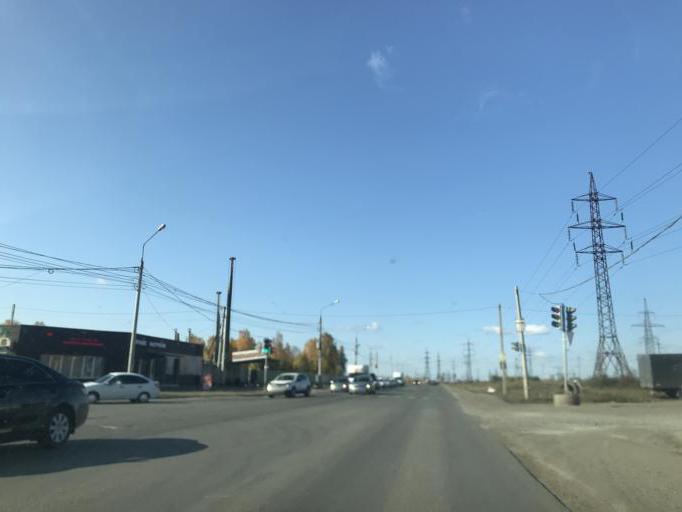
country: RU
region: Chelyabinsk
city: Roshchino
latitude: 55.2203
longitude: 61.2972
